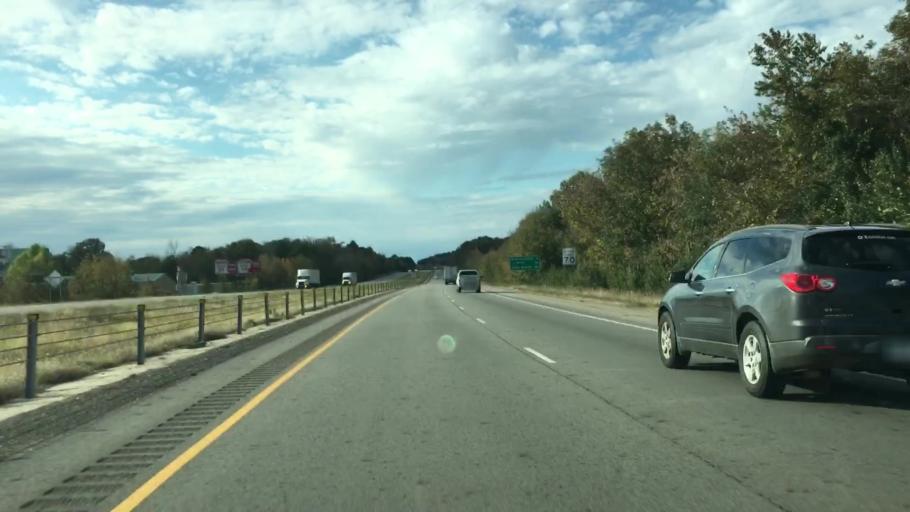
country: US
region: Arkansas
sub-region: Pope County
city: Pottsville
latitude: 35.2520
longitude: -93.0410
